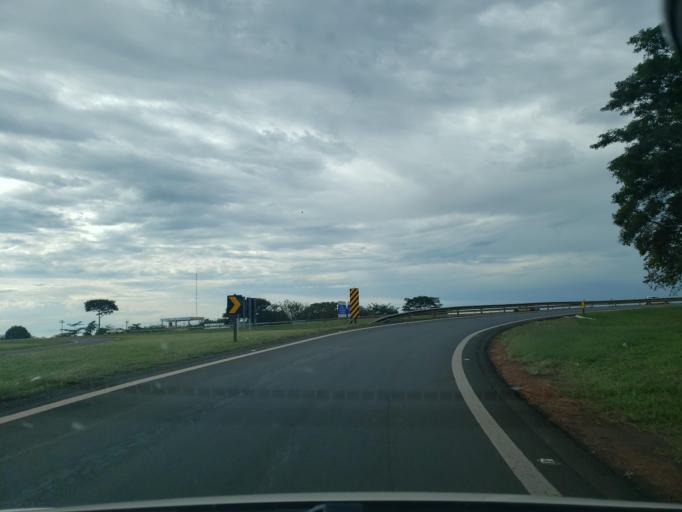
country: BR
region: Sao Paulo
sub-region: Jau
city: Jau
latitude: -22.2555
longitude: -48.5511
